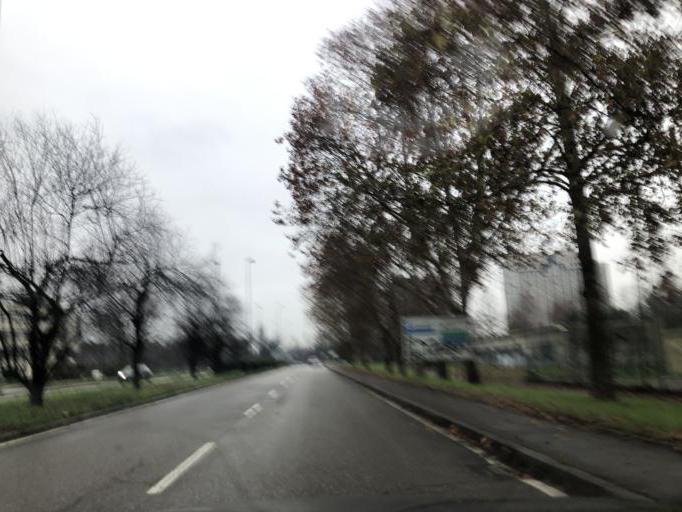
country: IT
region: Emilia-Romagna
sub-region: Provincia di Modena
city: Modena
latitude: 44.6373
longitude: 10.8994
